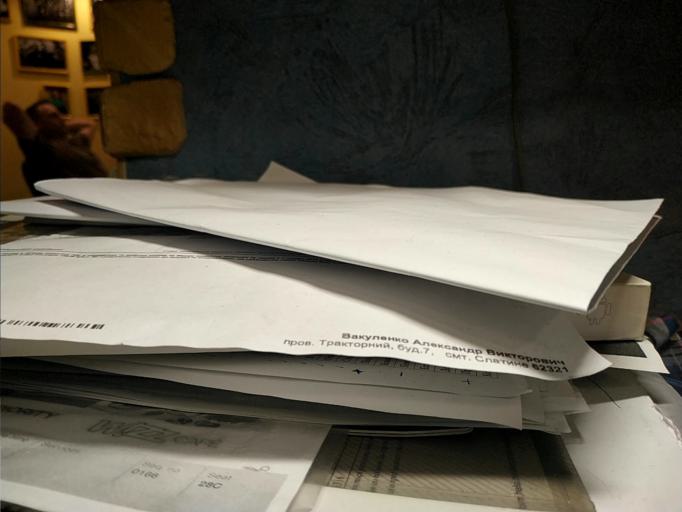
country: RU
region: Tverskaya
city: Zubtsov
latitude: 56.1104
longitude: 34.6296
